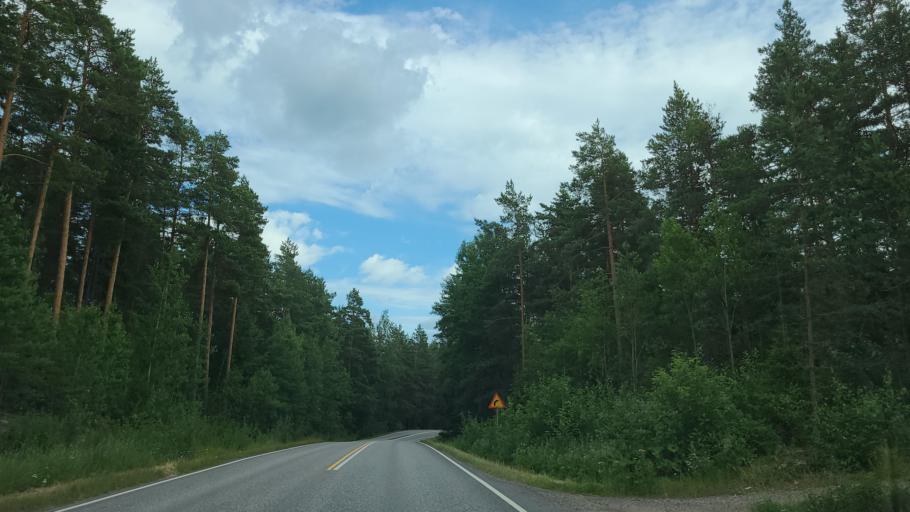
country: FI
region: Varsinais-Suomi
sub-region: Turku
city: Rymaettylae
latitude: 60.3631
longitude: 21.9509
